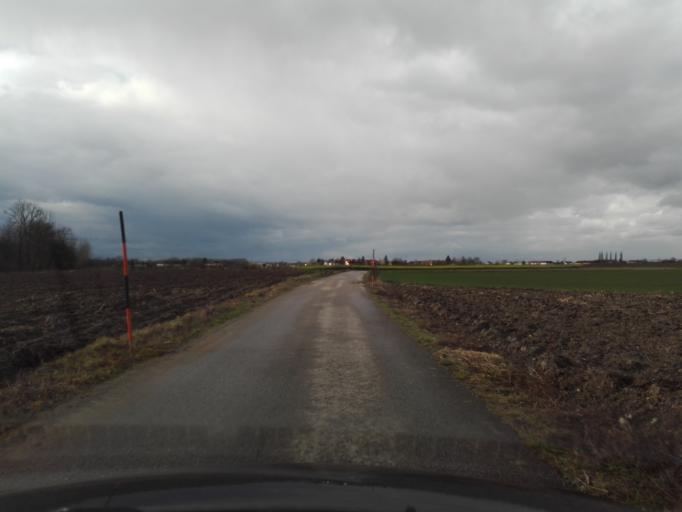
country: AT
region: Lower Austria
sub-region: Politischer Bezirk Amstetten
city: Strengberg
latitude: 48.1769
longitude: 14.6905
